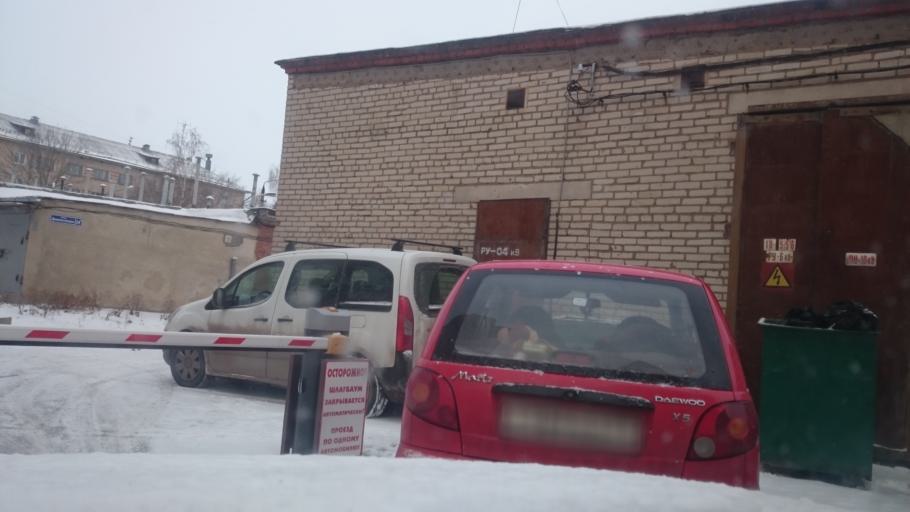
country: RU
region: Tula
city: Tula
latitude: 54.1925
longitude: 37.5993
